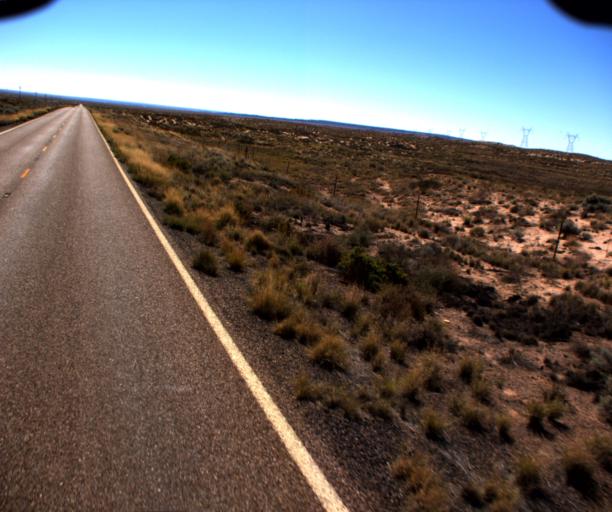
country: US
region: Arizona
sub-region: Navajo County
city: Holbrook
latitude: 35.1564
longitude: -110.0836
